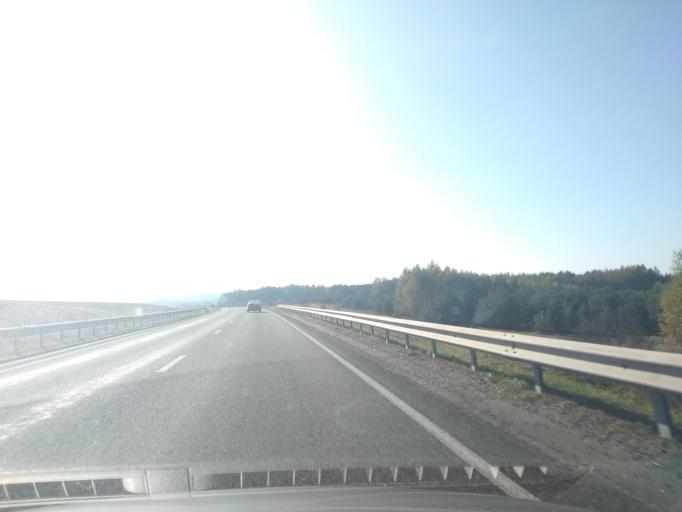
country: BY
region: Grodnenskaya
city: Zhyrovichy
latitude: 53.0604
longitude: 25.3898
